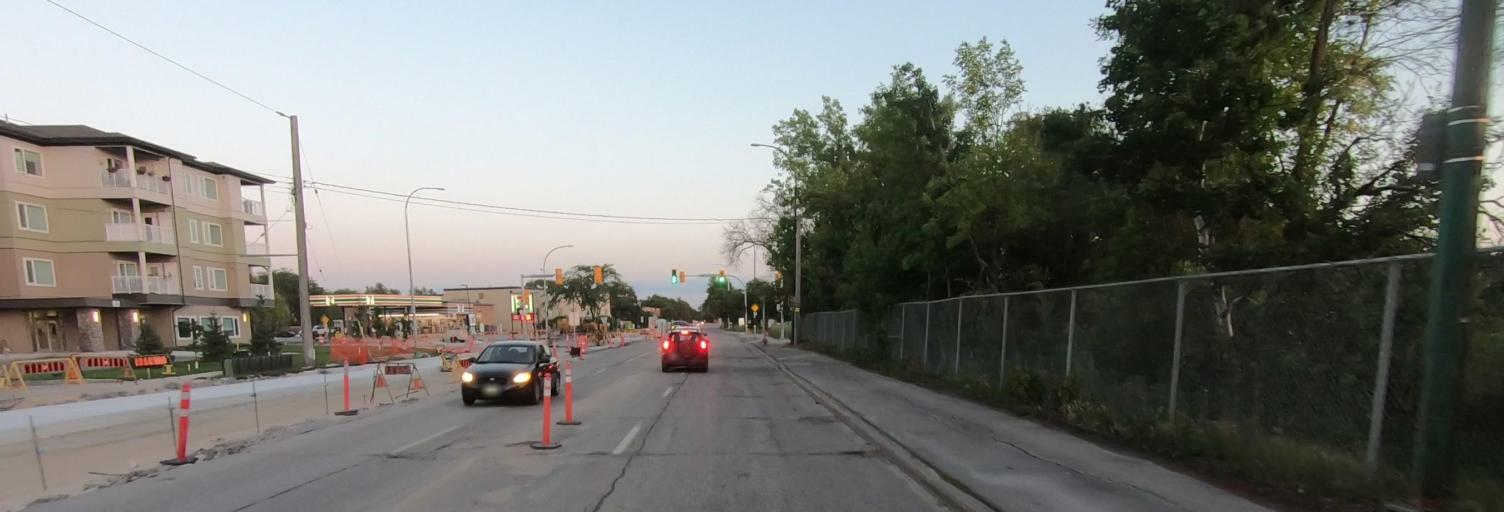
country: CA
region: Manitoba
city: Winnipeg
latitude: 49.8717
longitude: -97.0938
